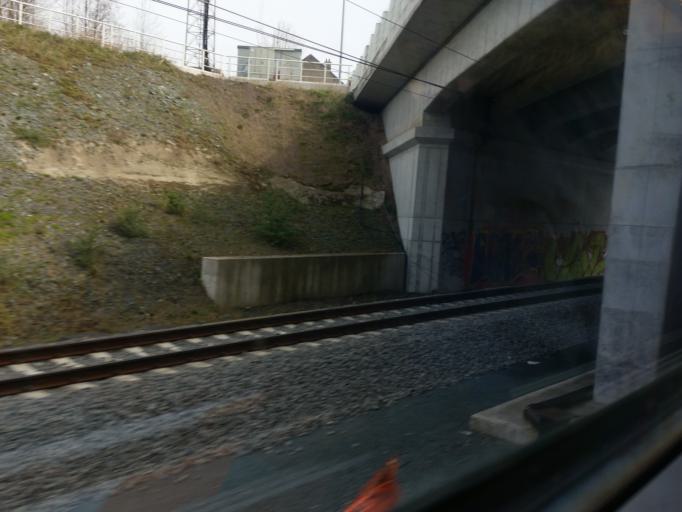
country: BE
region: Flanders
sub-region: Provincie Vlaams-Brabant
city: Sint-Martens-Lennik
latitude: 50.8393
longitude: 4.2074
